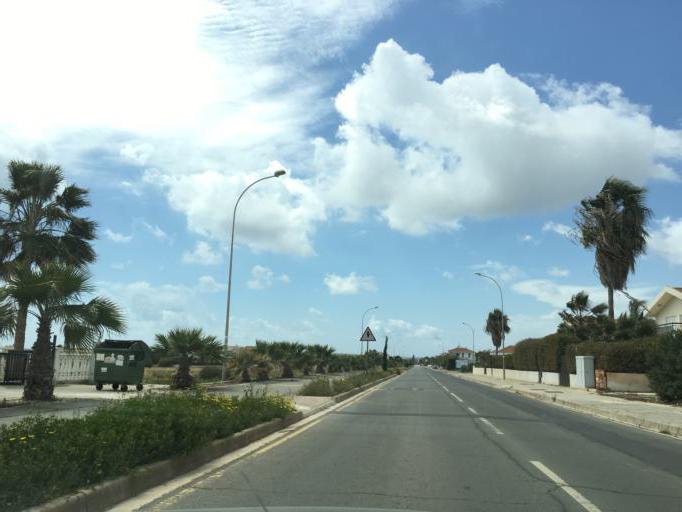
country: CY
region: Ammochostos
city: Liopetri
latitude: 34.9803
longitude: 33.9252
